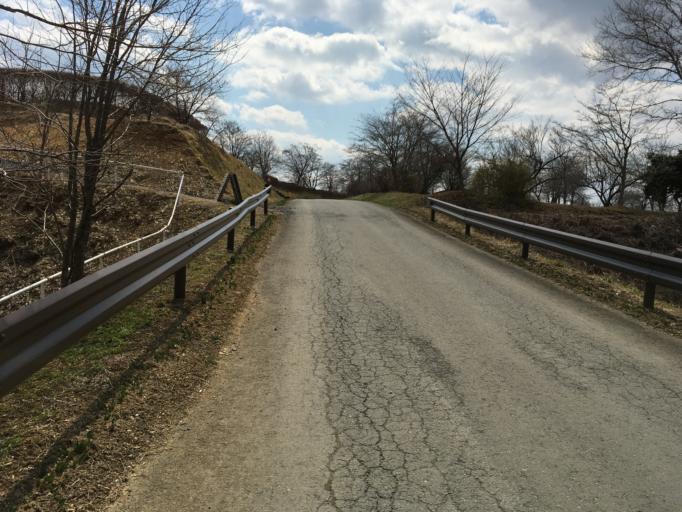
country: JP
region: Iwate
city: Ichinoseki
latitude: 38.8187
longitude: 141.2720
